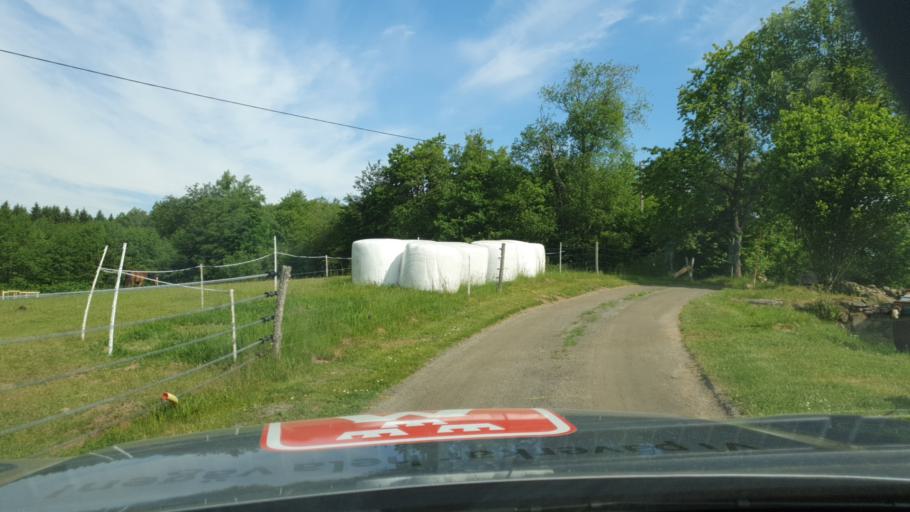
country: SE
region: Skane
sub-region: Hassleholms Kommun
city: Vinslov
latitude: 56.0435
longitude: 13.8672
